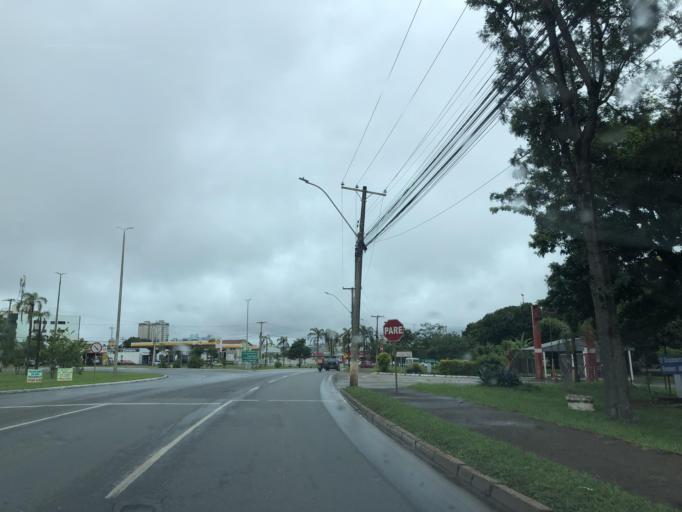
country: BR
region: Federal District
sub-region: Brasilia
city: Brasilia
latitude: -15.8588
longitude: -48.0683
